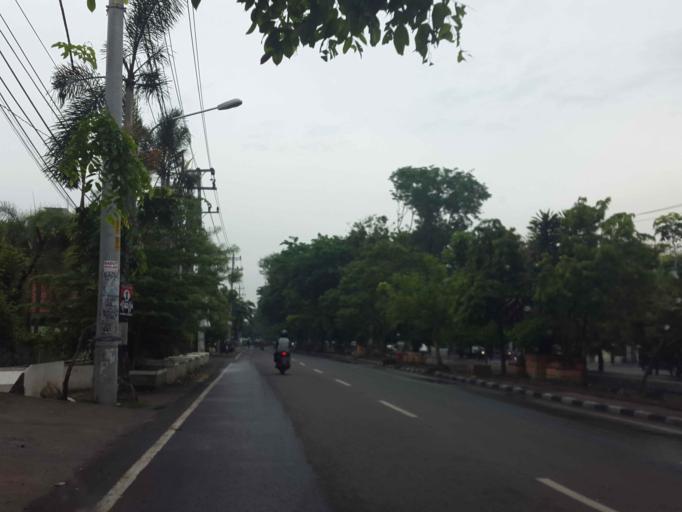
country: ID
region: Central Java
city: Semarang
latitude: -6.9858
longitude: 110.4227
